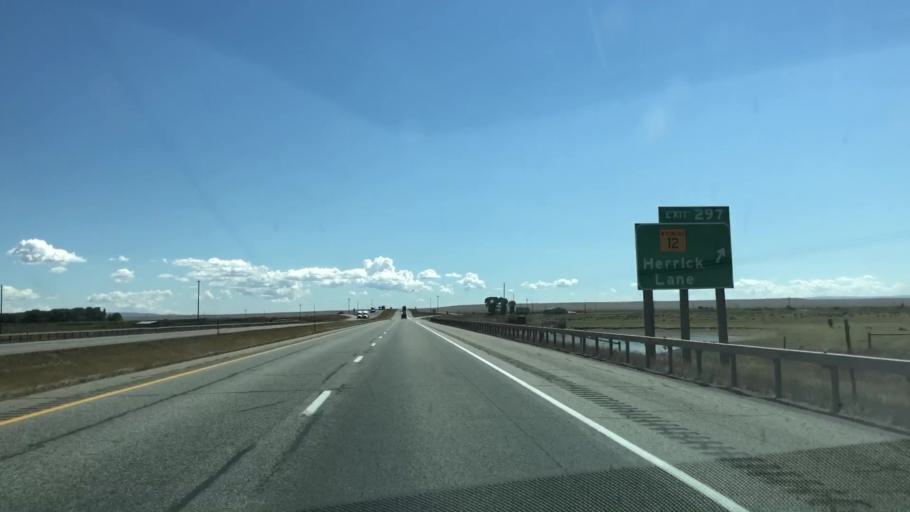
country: US
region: Wyoming
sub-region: Albany County
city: Laramie
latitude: 41.4017
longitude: -105.8300
